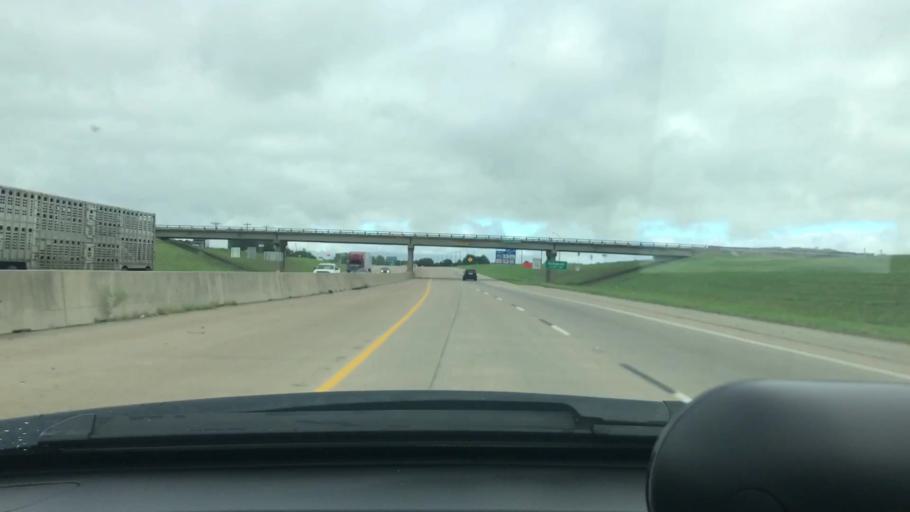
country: US
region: Texas
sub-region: Grayson County
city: Van Alstyne
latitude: 33.3989
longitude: -96.5802
